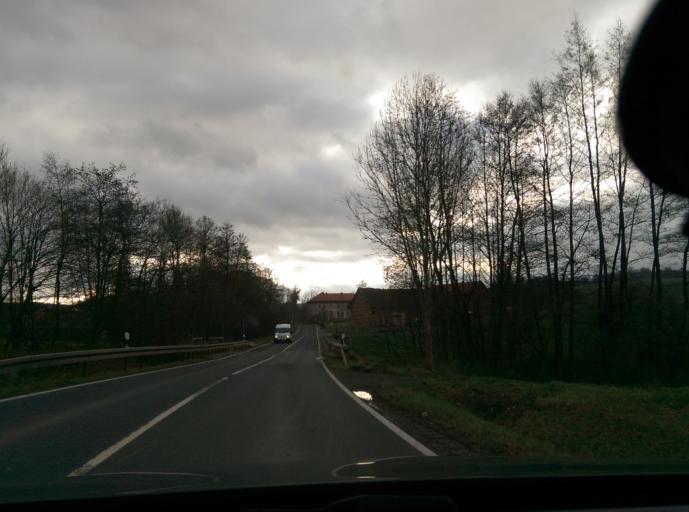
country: DE
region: Thuringia
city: Krauthausen
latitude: 51.0281
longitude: 10.2580
